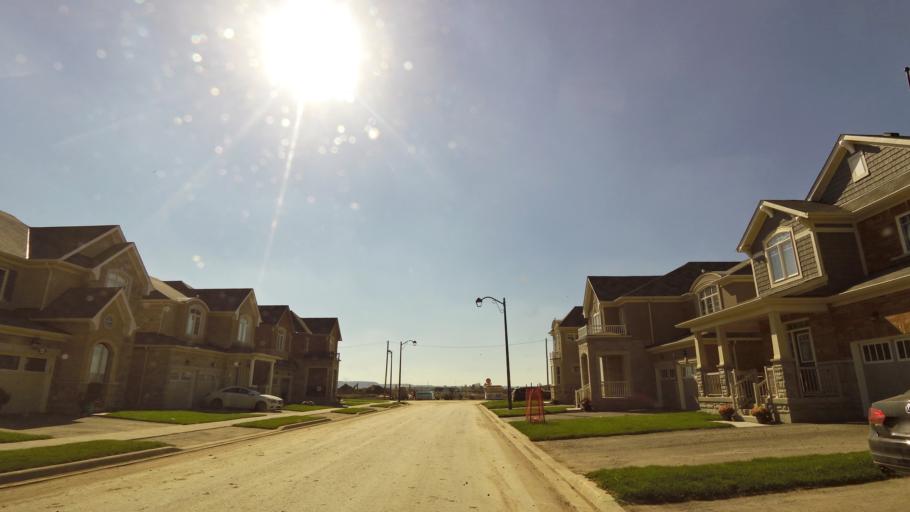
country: CA
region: Ontario
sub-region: Halton
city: Milton
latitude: 43.4856
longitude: -79.8429
